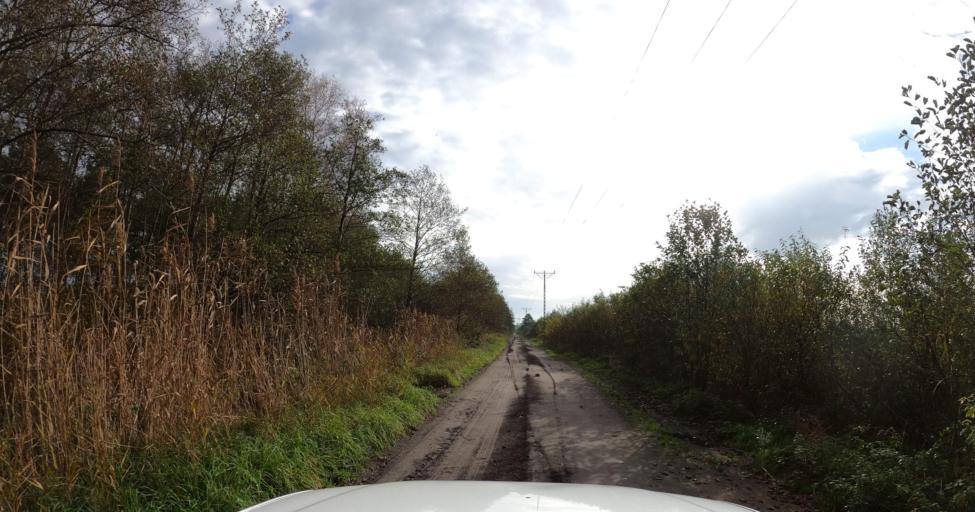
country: PL
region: West Pomeranian Voivodeship
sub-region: Powiat kamienski
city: Kamien Pomorski
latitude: 53.9890
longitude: 14.8460
